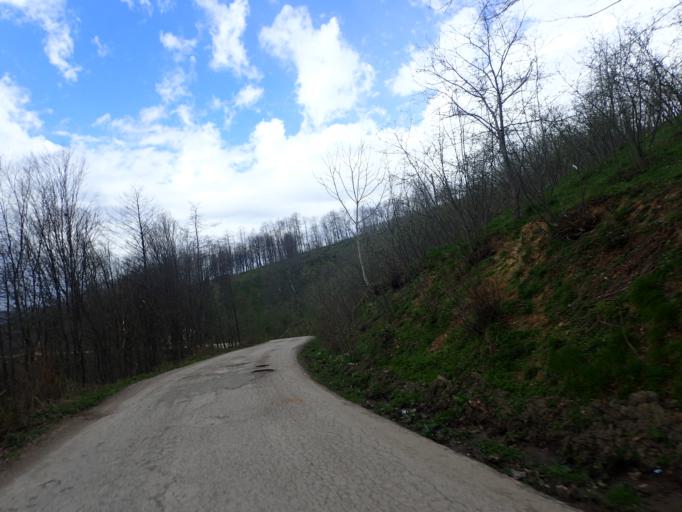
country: TR
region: Ordu
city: Korgan
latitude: 40.7925
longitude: 37.2819
